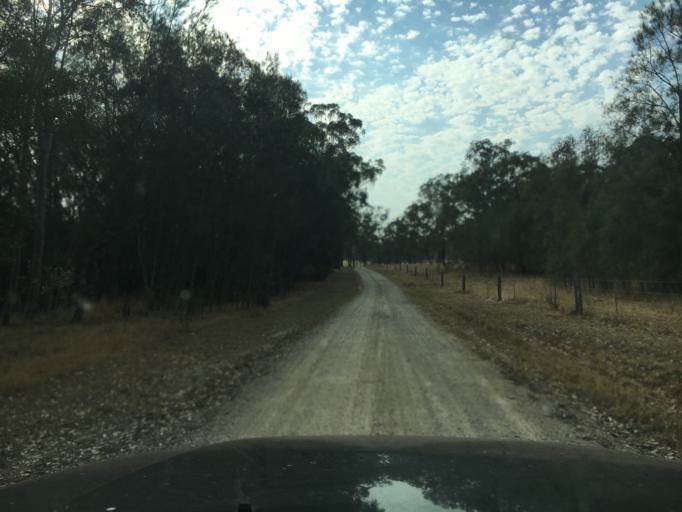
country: AU
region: New South Wales
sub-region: Cessnock
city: Branxton
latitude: -32.6652
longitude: 151.3003
